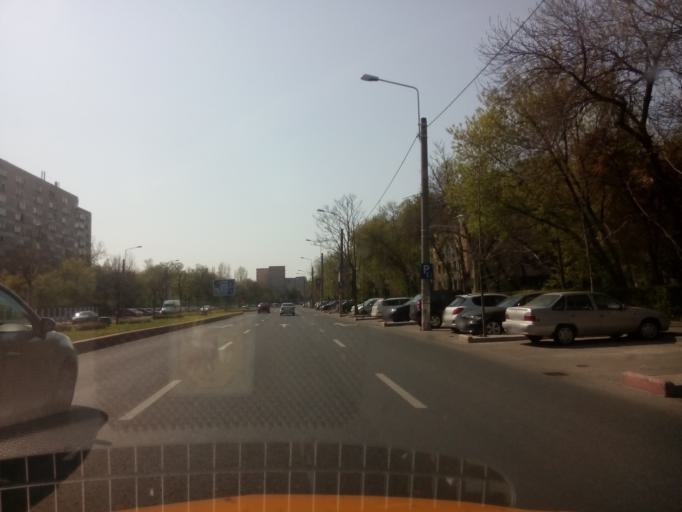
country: RO
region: Ilfov
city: Dobroesti
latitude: 44.4204
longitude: 26.1643
